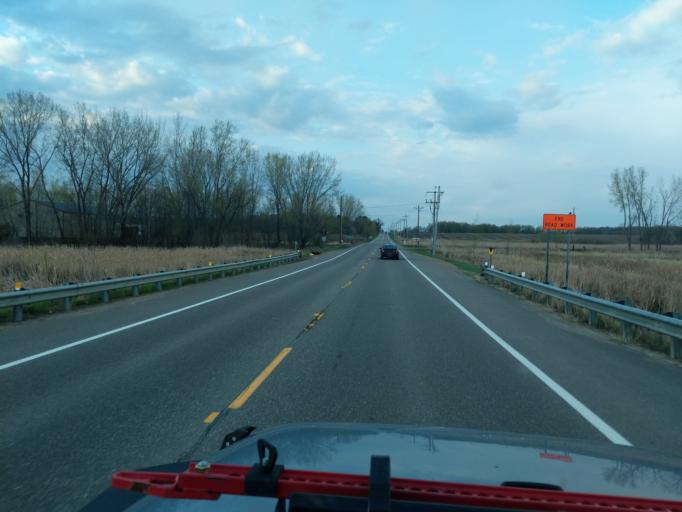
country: US
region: Minnesota
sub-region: Hennepin County
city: Rogers
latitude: 45.1541
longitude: -93.5219
